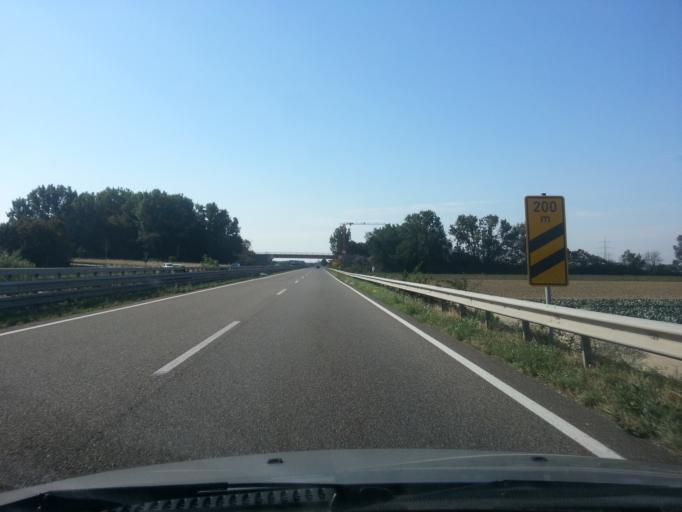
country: DE
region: Rheinland-Pfalz
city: Bobenheim-Roxheim
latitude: 49.5702
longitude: 8.3976
